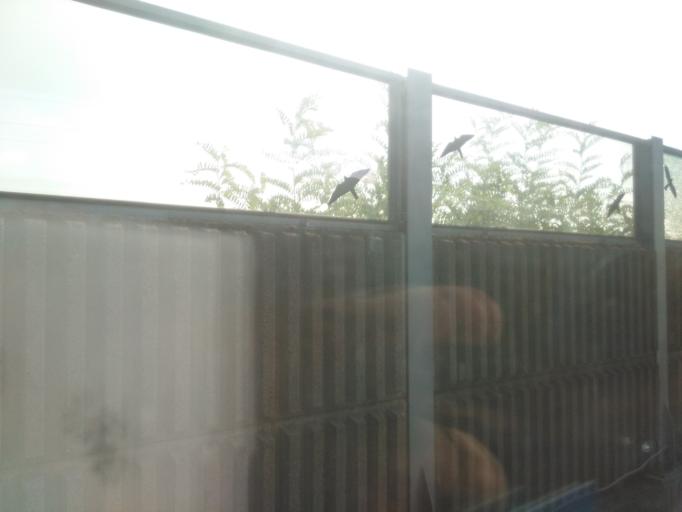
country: IT
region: Lombardy
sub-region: Citta metropolitana di Milano
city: Cassano d'Adda
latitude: 45.5099
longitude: 9.5175
